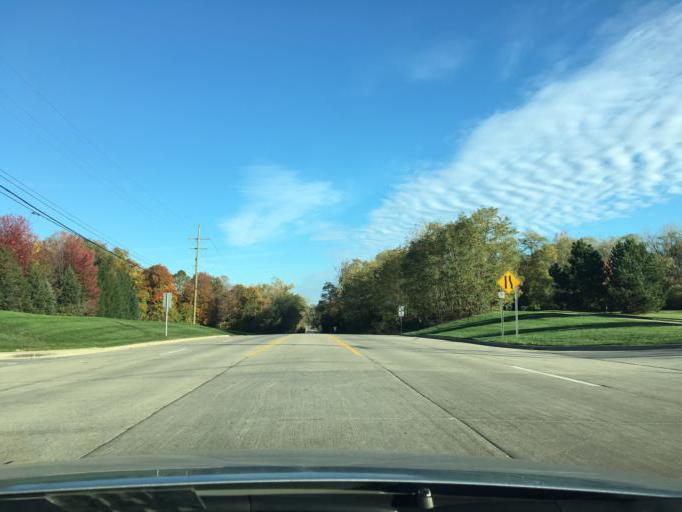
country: US
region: Michigan
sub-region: Wayne County
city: Northville
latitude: 42.4027
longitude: -83.4819
